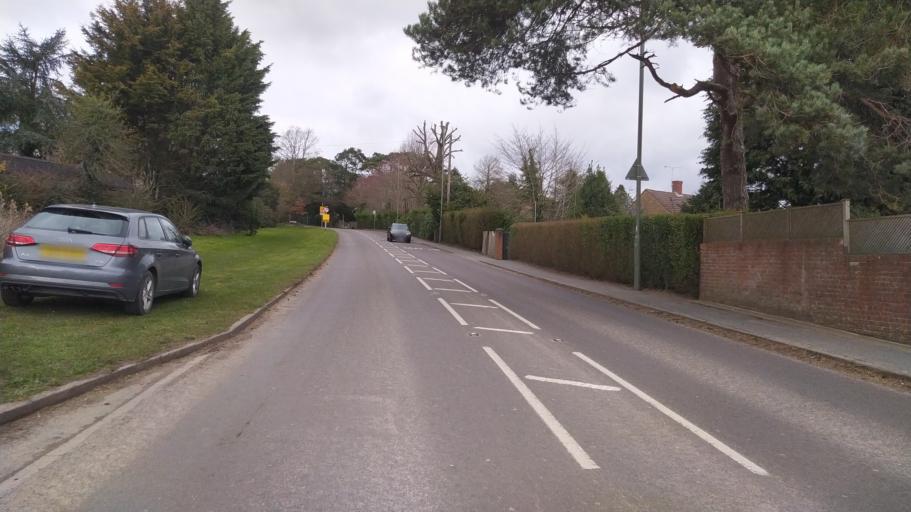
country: GB
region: England
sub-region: Surrey
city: Farnham
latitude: 51.2330
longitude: -0.8107
